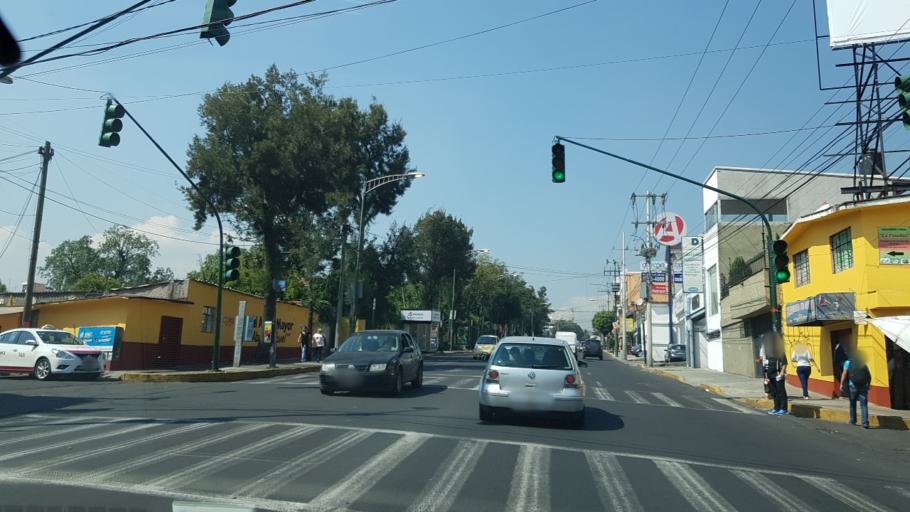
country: MX
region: Mexico City
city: Magdalena Contreras
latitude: 19.3498
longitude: -99.2229
